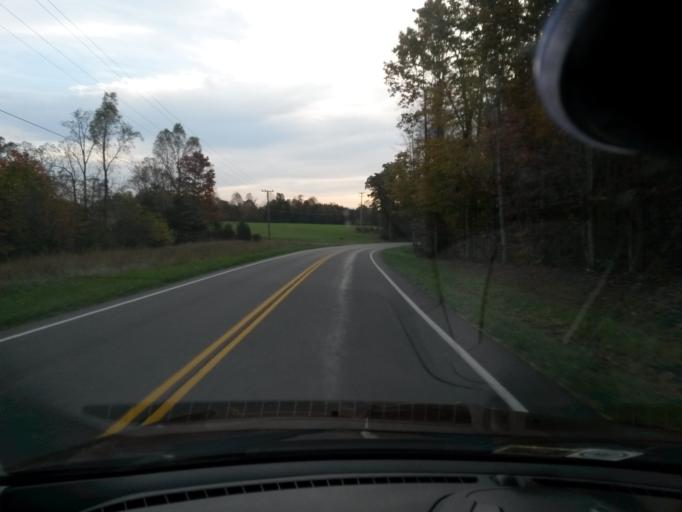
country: US
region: Virginia
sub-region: Franklin County
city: North Shore
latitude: 37.1248
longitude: -79.7425
